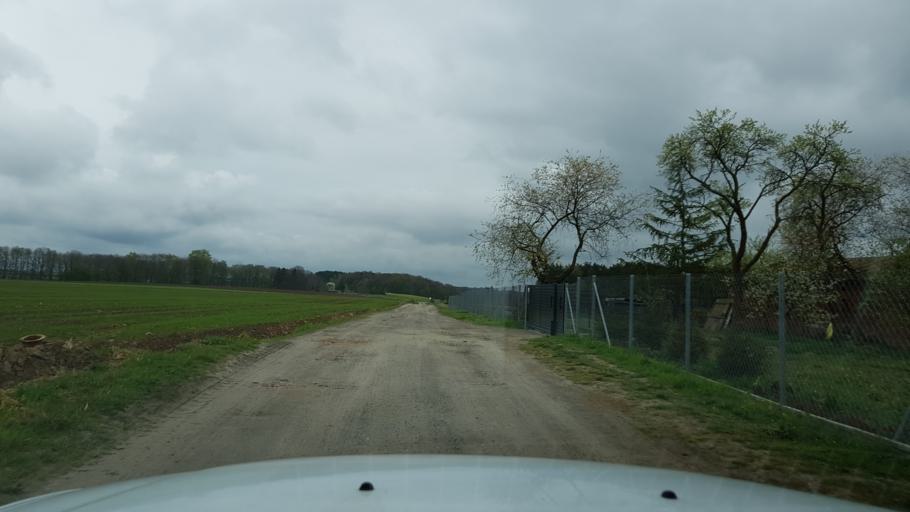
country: PL
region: West Pomeranian Voivodeship
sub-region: Powiat kolobrzeski
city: Ryman
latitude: 54.0329
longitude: 15.4806
